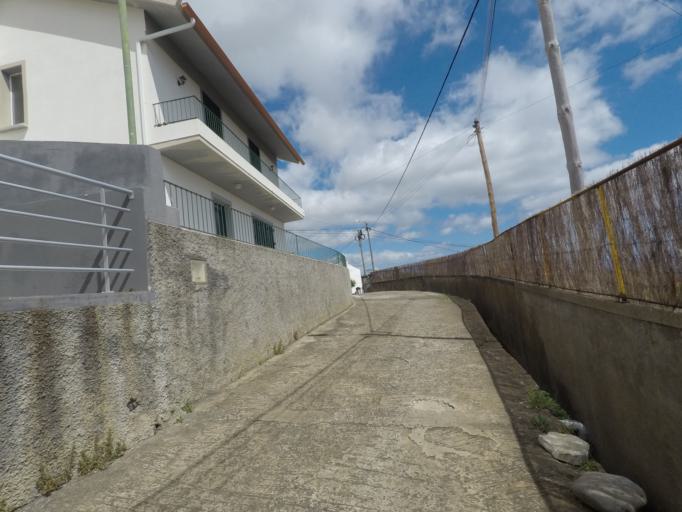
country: PT
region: Madeira
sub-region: Calheta
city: Estreito da Calheta
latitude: 32.7348
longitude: -17.1839
